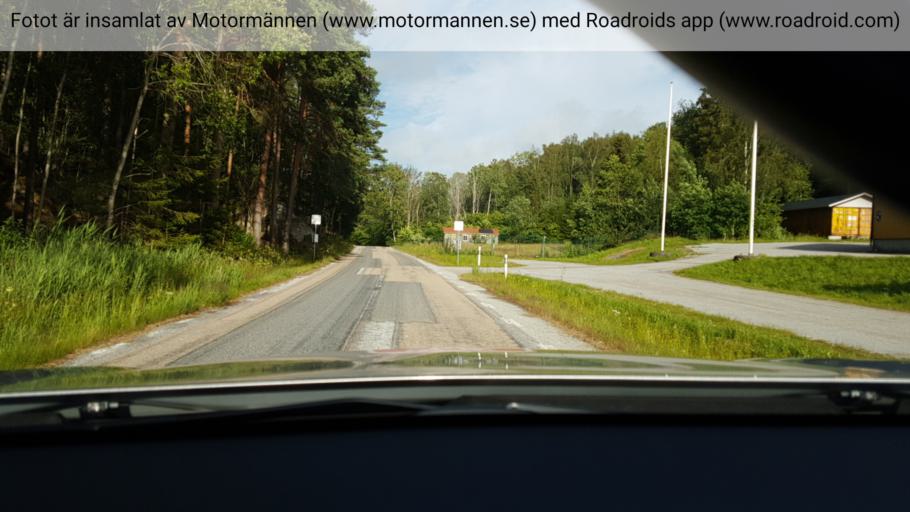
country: SE
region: Vaestra Goetaland
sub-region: Tjorns Kommun
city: Myggenas
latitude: 58.1264
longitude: 11.6763
